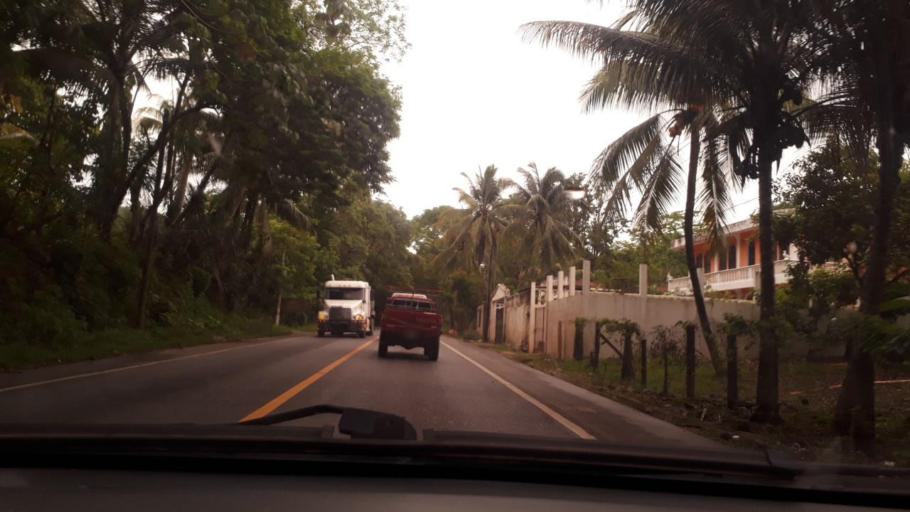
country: GT
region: Izabal
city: Morales
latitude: 15.5377
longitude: -88.7514
